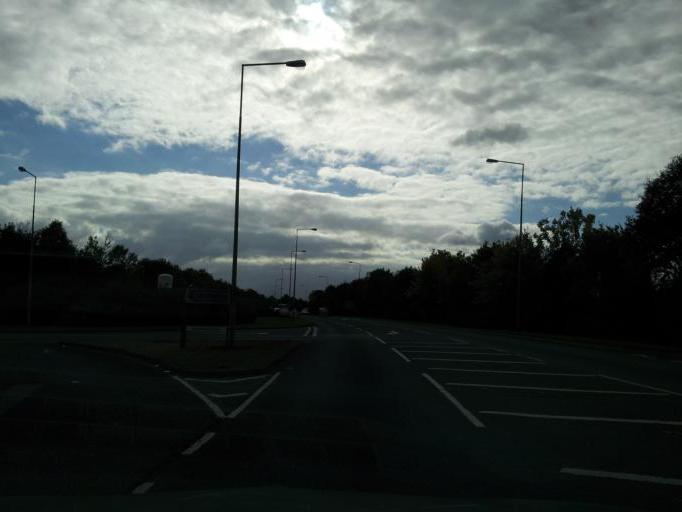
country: GB
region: England
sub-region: Milton Keynes
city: Shenley Church End
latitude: 52.0010
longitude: -0.7955
